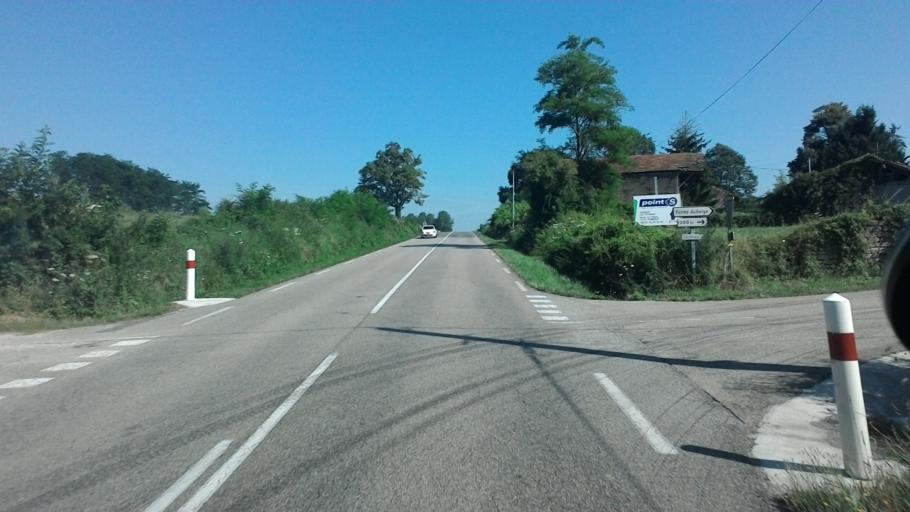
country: FR
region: Bourgogne
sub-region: Departement de Saone-et-Loire
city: Romenay
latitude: 46.4857
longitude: 5.0715
